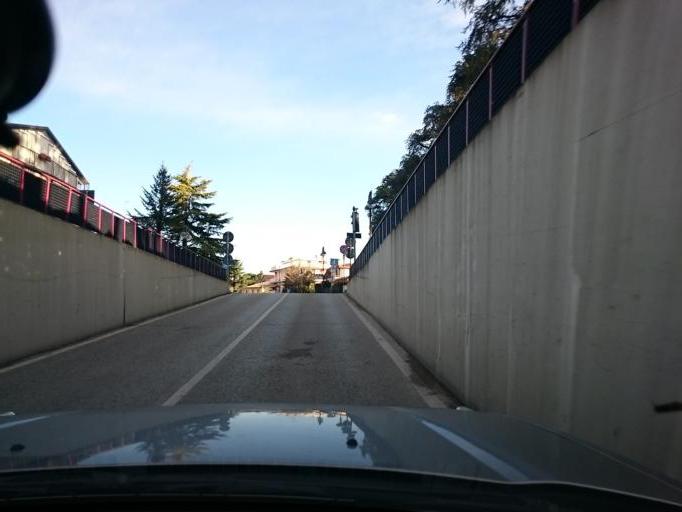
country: IT
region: Veneto
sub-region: Provincia di Padova
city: Montegrotto Terme
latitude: 45.3268
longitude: 11.7967
